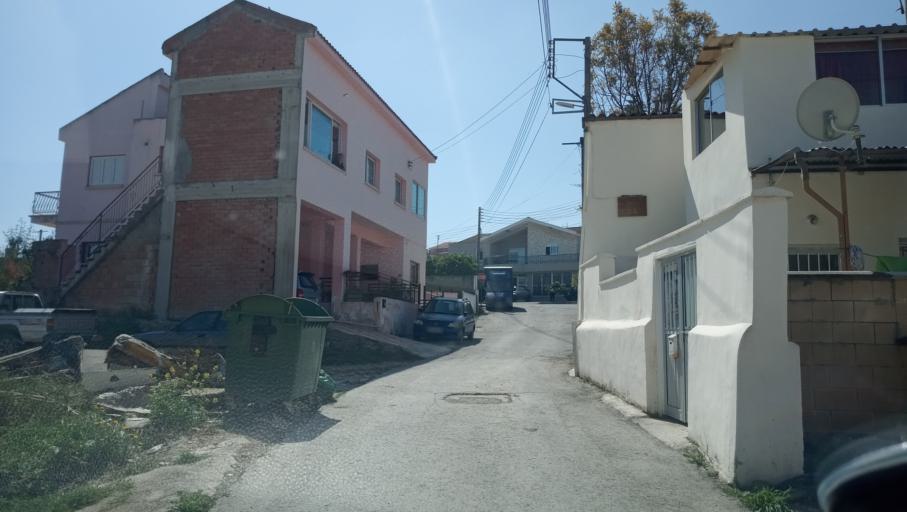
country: CY
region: Lefkosia
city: Alampra
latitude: 35.0144
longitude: 33.3876
